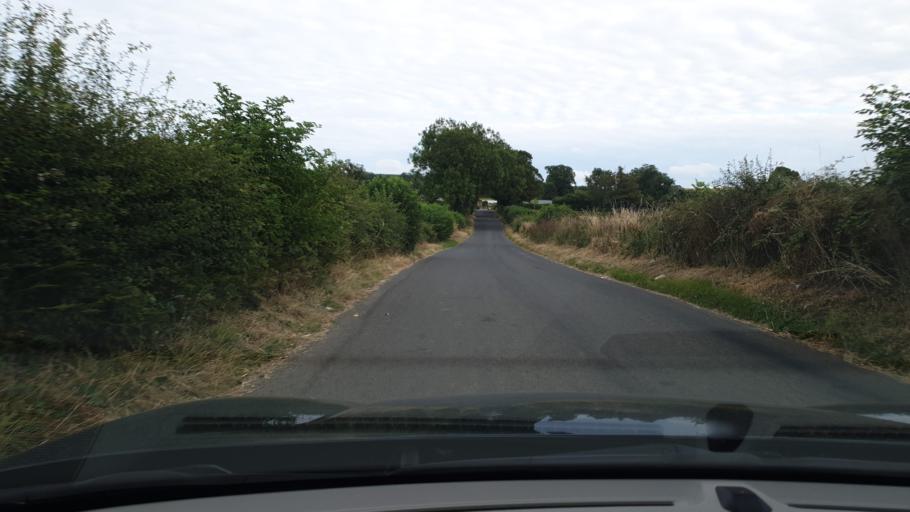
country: IE
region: Leinster
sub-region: An Mhi
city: Stamullin
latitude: 53.5831
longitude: -6.3093
